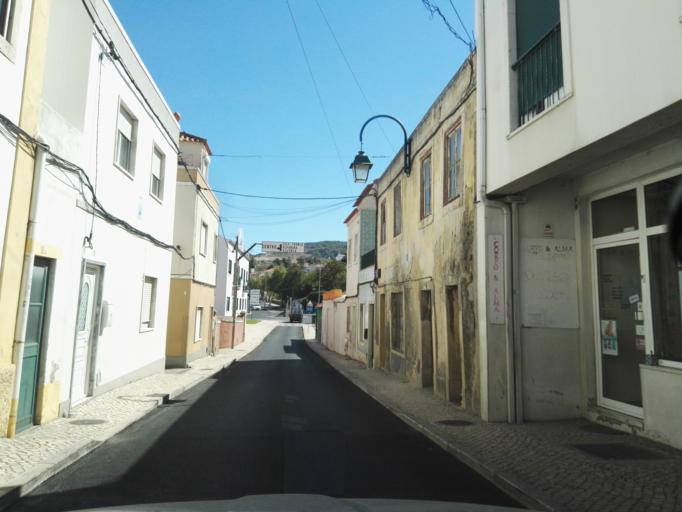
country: PT
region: Lisbon
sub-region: Arruda Dos Vinhos
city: Arruda dos Vinhos
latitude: 38.9814
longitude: -9.0778
